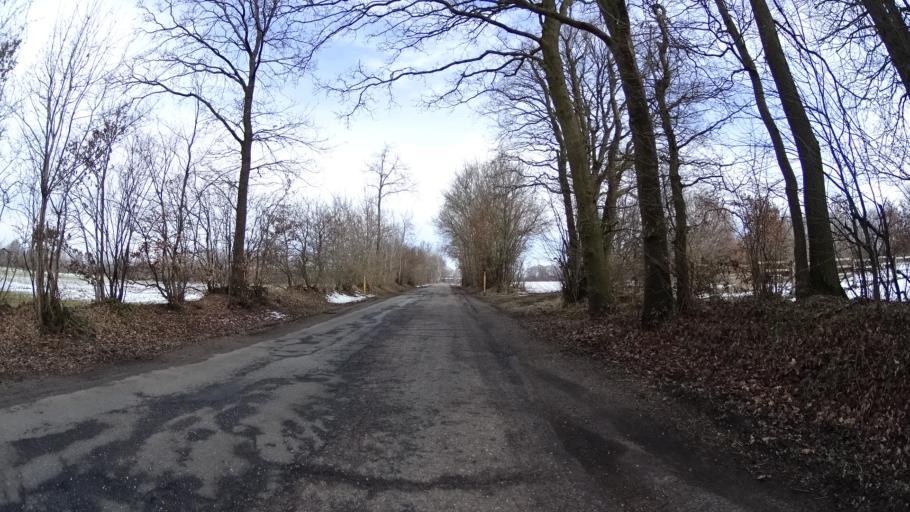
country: DE
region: Schleswig-Holstein
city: Gross Kummerfeld
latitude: 54.0309
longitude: 10.1143
